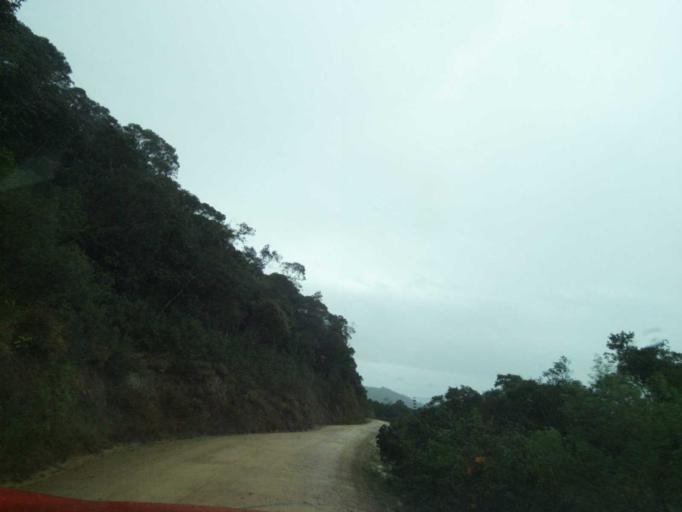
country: BR
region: Santa Catarina
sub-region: Anitapolis
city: Anitapolis
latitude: -27.9220
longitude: -49.1794
